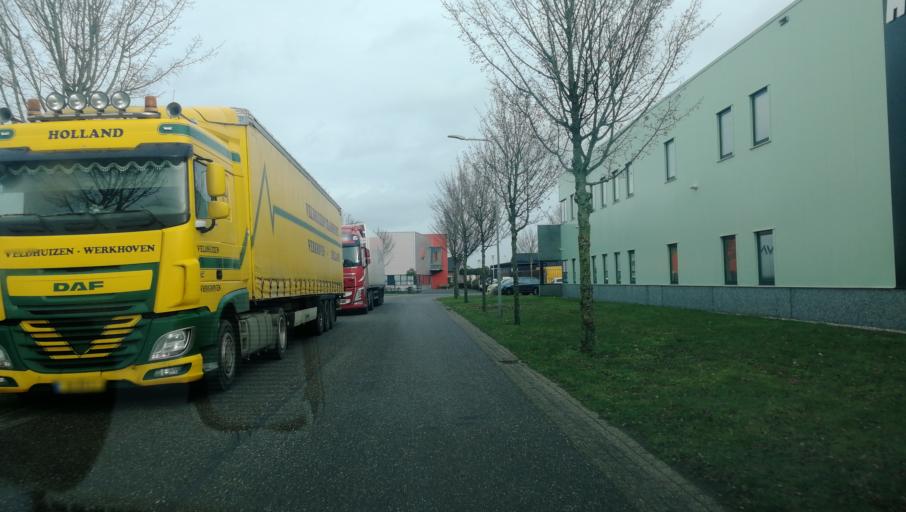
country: NL
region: Limburg
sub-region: Gemeente Venlo
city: Tegelen
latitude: 51.3227
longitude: 6.1252
